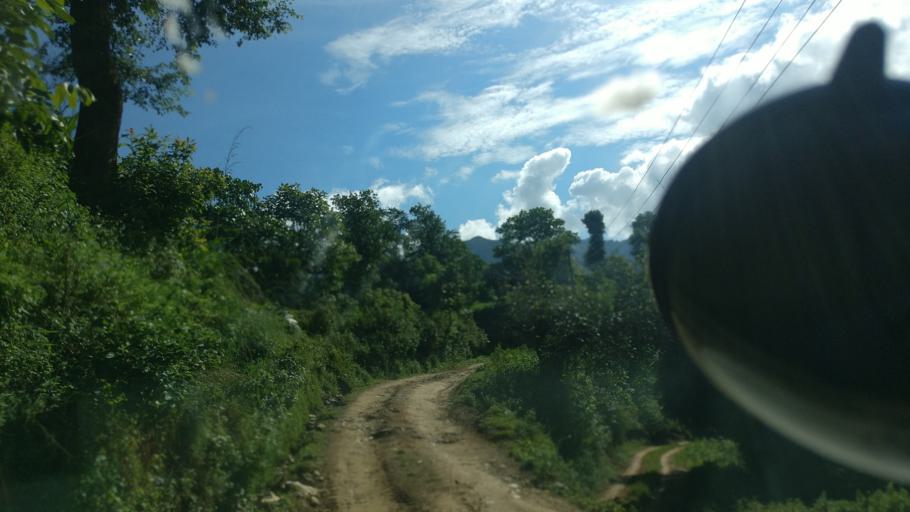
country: NP
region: Western Region
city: Baglung
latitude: 28.1338
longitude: 83.6576
